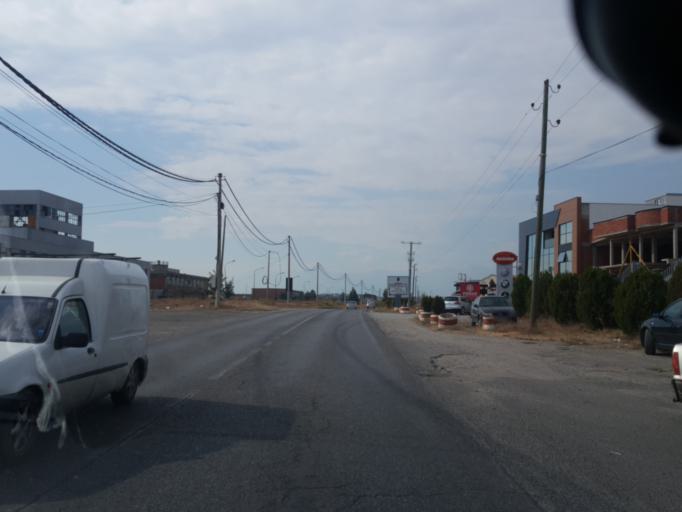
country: XK
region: Gjakova
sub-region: Komuna e Gjakoves
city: Gjakove
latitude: 42.3685
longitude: 20.4597
